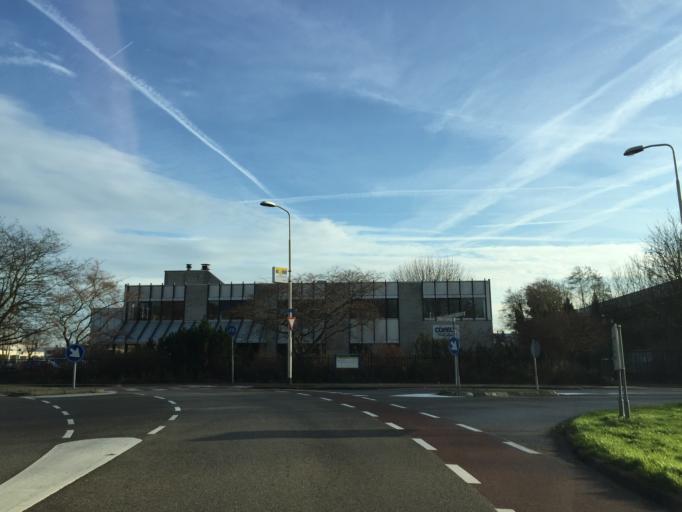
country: NL
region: South Holland
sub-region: Gemeente Zoetermeer
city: Zoetermeer
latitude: 52.0486
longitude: 4.5043
